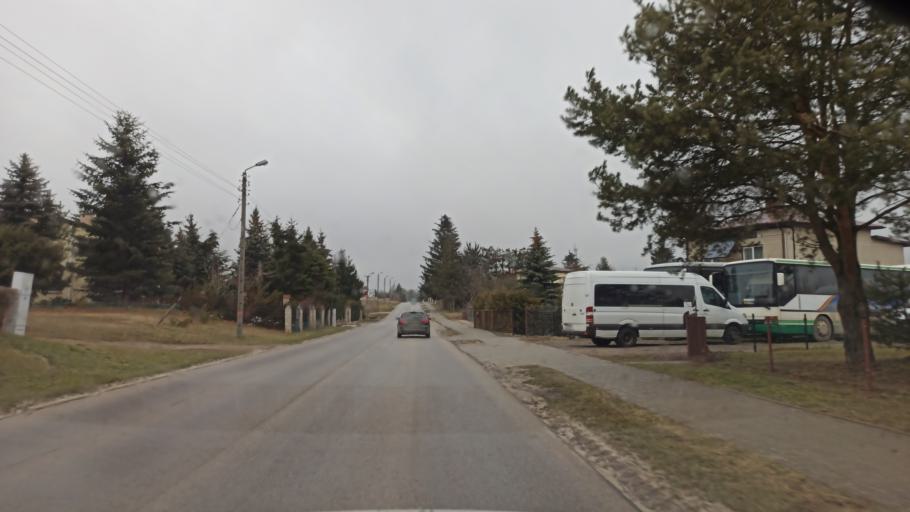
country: PL
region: Lublin Voivodeship
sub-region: Powiat lubelski
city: Bychawa
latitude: 51.0073
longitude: 22.5515
